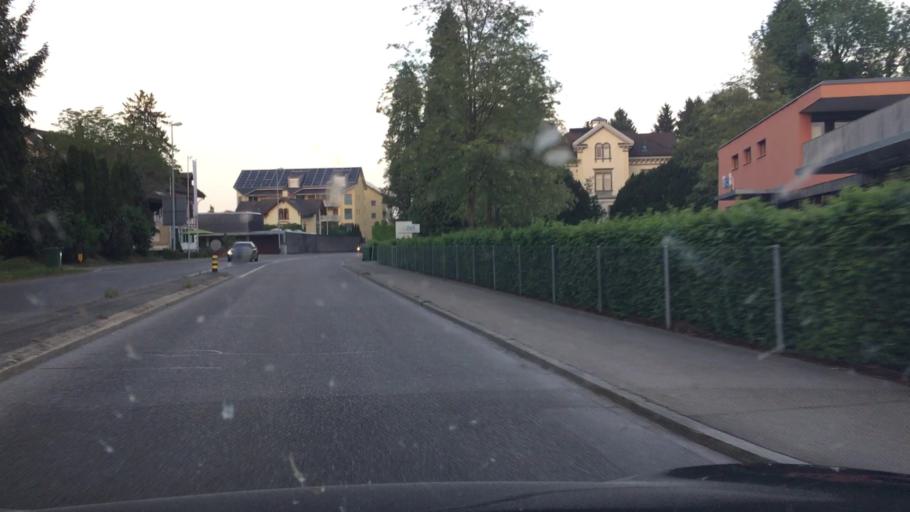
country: CH
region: Thurgau
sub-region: Frauenfeld District
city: Mullheim
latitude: 47.5999
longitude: 8.9963
